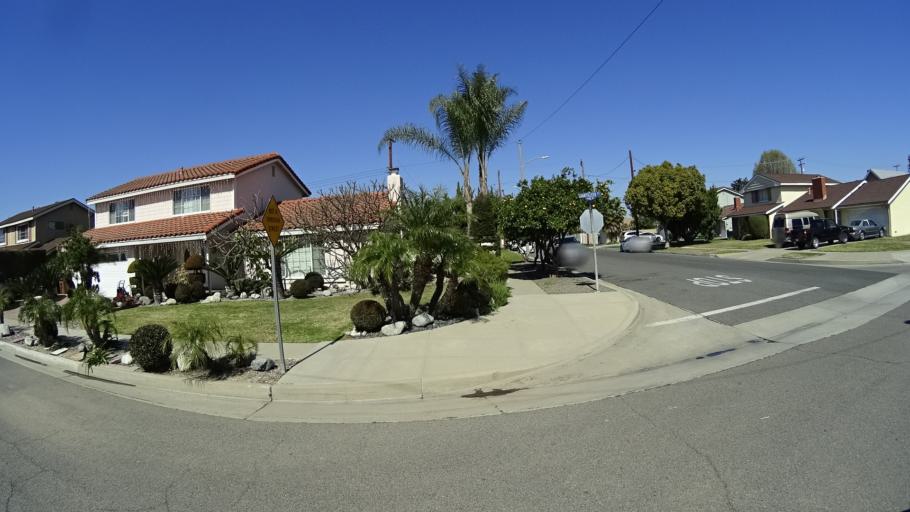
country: US
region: California
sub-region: Orange County
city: Anaheim
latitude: 33.8127
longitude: -117.9394
